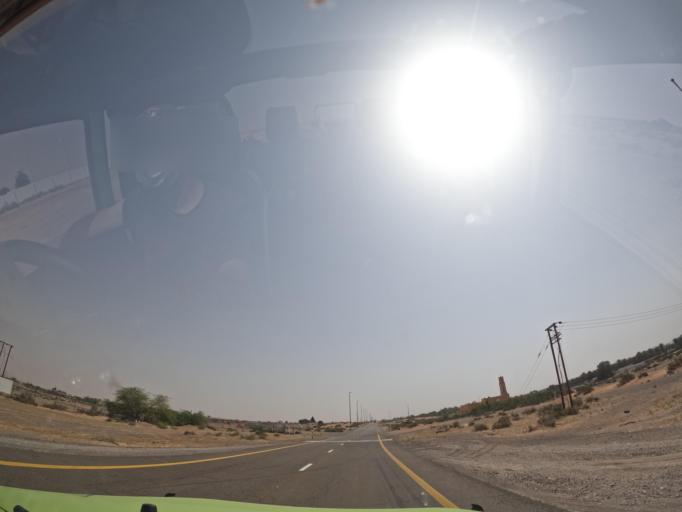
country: OM
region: Al Buraimi
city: Al Buraymi
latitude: 24.6888
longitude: 55.5959
